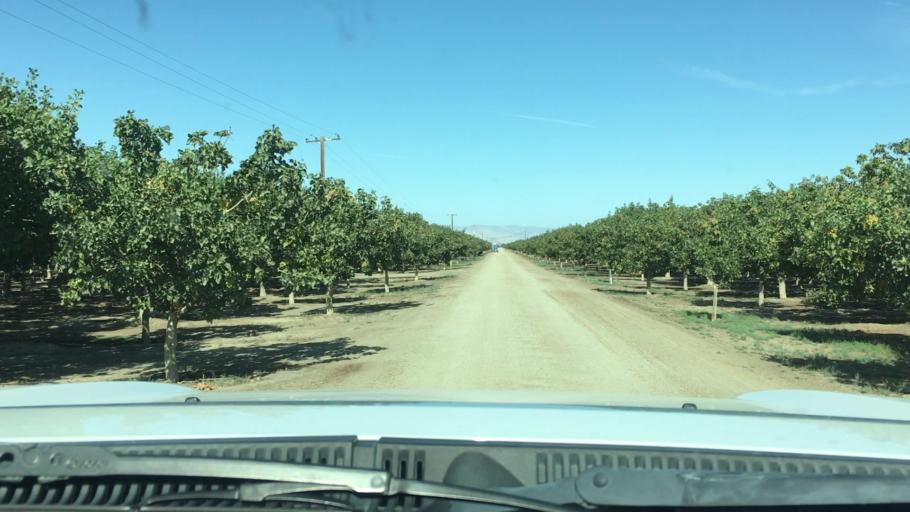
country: US
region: California
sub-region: Kern County
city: Buttonwillow
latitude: 35.3694
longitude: -119.3887
